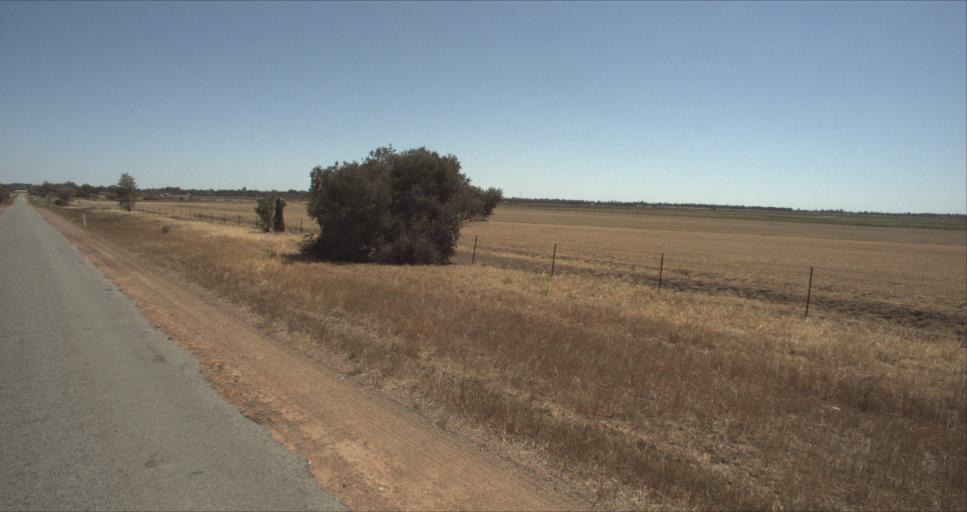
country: AU
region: New South Wales
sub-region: Leeton
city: Leeton
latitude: -34.5408
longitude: 146.4379
